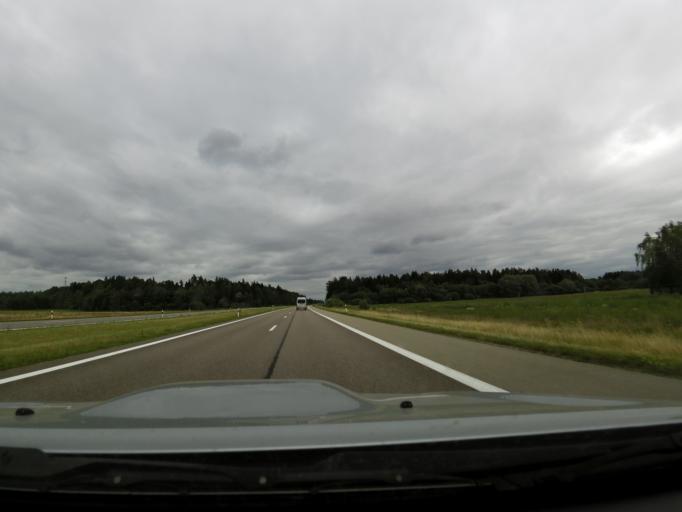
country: LT
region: Vilnius County
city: Ukmerge
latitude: 55.5092
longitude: 24.6082
